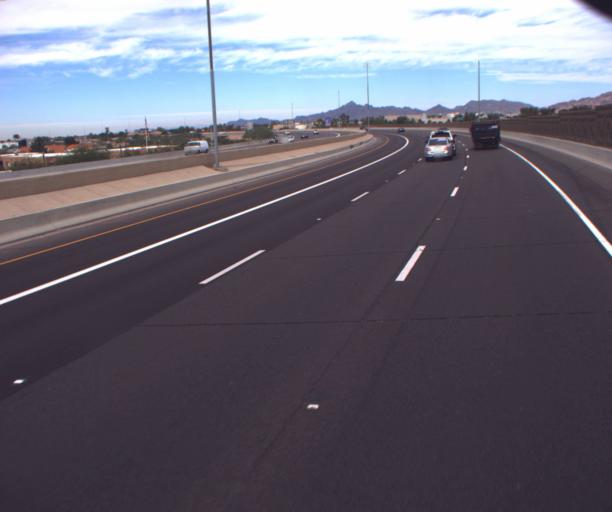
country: US
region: Arizona
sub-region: Maricopa County
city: Tempe Junction
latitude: 33.4513
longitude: -111.9688
